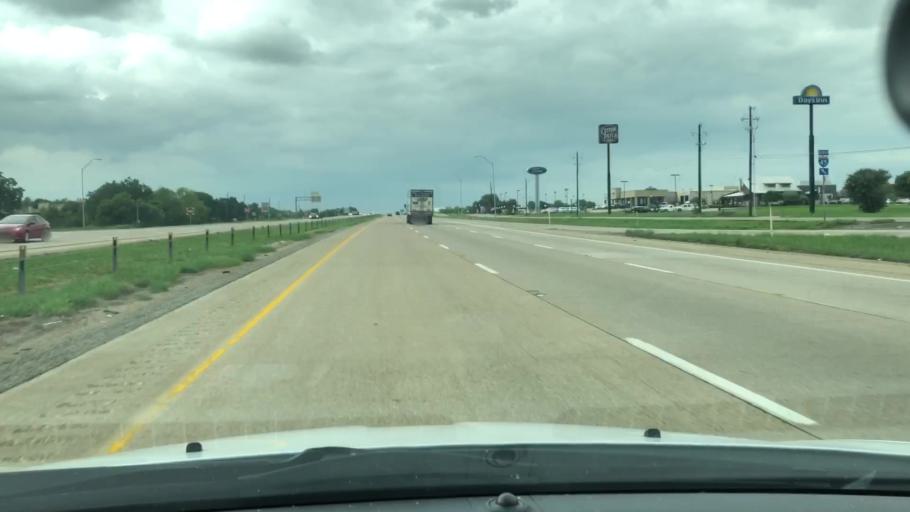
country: US
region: Texas
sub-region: Ellis County
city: Ennis
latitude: 32.3380
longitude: -96.6181
